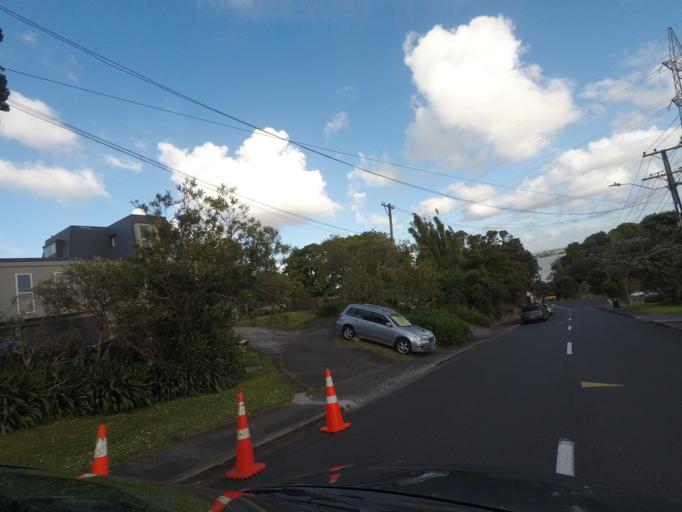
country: NZ
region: Auckland
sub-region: Auckland
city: Mangere
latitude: -36.9284
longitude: 174.7584
